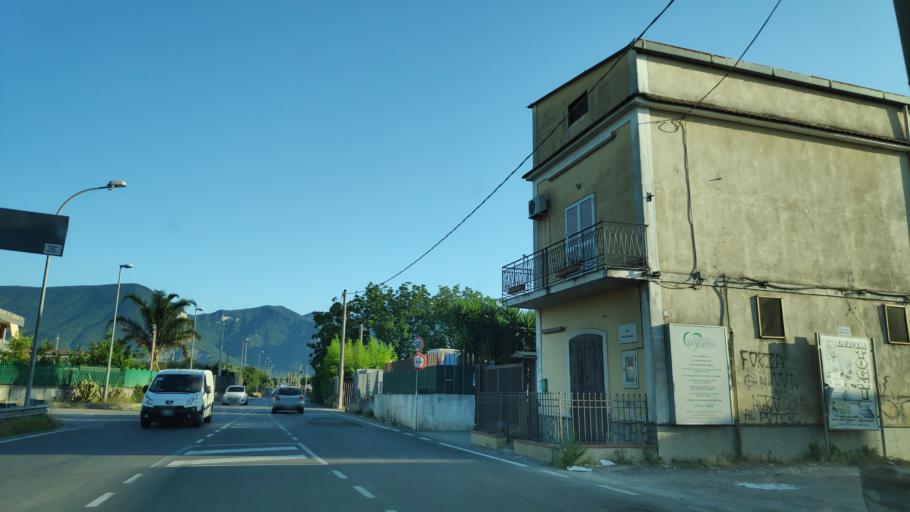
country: IT
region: Campania
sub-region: Provincia di Salerno
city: San Valentino Torio
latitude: 40.7745
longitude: 14.6110
